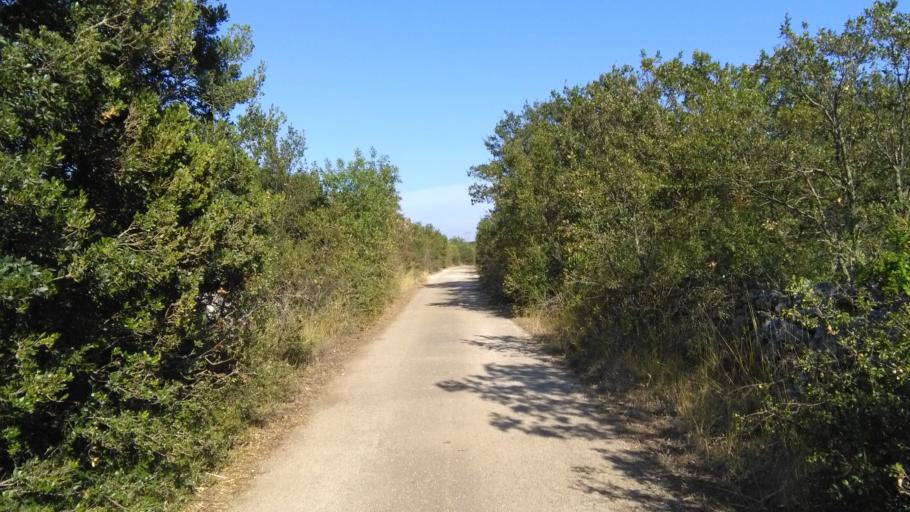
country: IT
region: Apulia
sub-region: Provincia di Bari
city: Putignano
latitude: 40.8204
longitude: 17.0395
